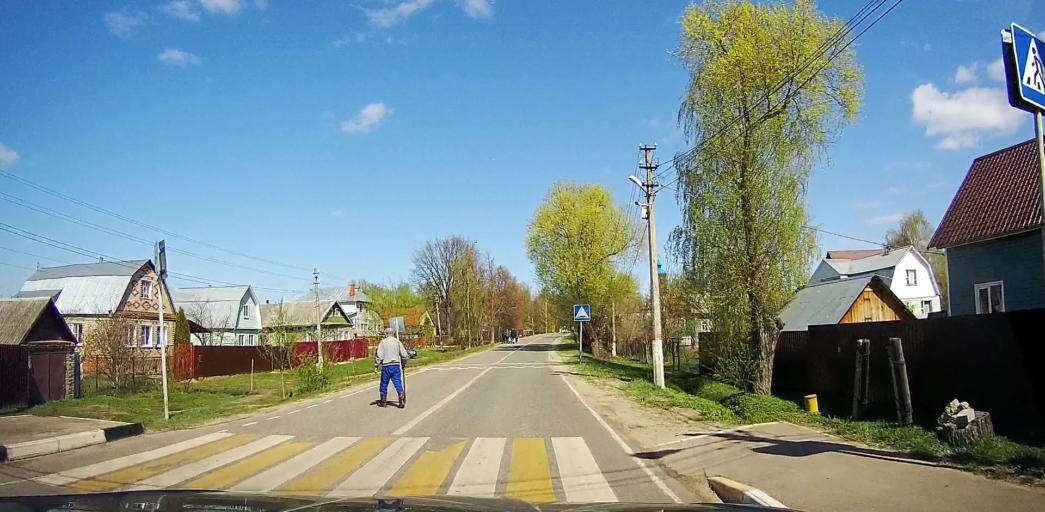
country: RU
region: Moskovskaya
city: Ramenskoye
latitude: 55.6240
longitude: 38.3022
